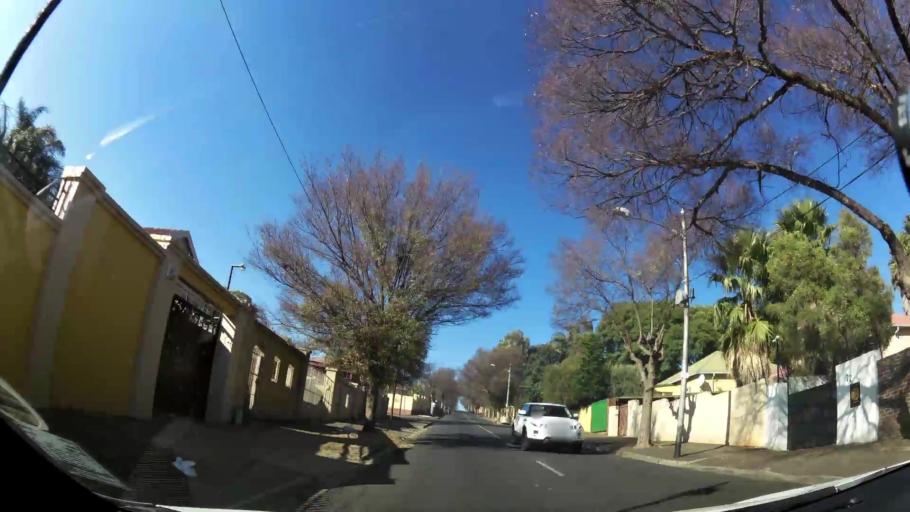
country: ZA
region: Gauteng
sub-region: City of Johannesburg Metropolitan Municipality
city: Johannesburg
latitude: -26.1972
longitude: 28.0973
